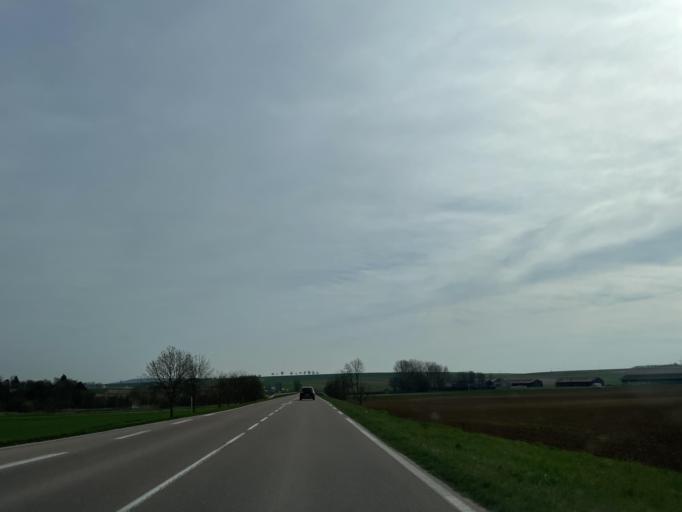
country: FR
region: Champagne-Ardenne
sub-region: Departement de l'Aube
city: Nogent-sur-Seine
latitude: 48.4826
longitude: 3.4955
